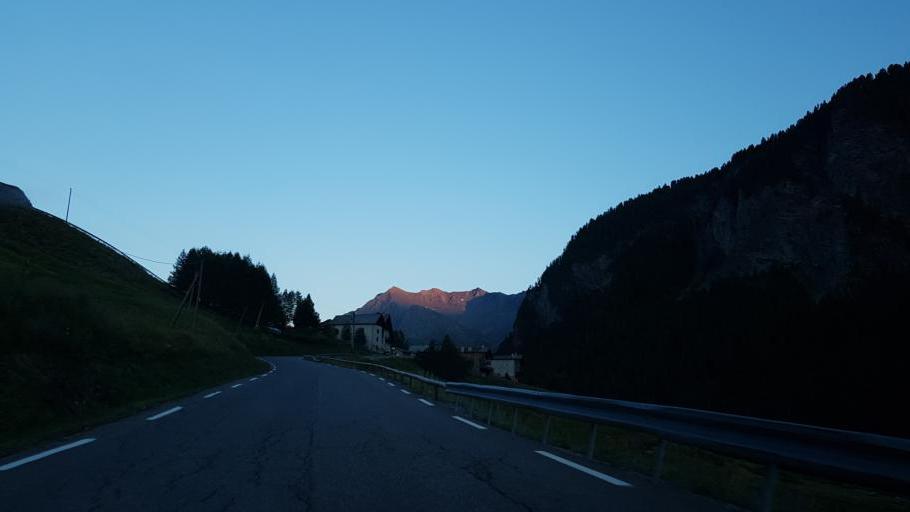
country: IT
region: Piedmont
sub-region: Provincia di Cuneo
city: Pontechianale
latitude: 44.7007
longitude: 6.8598
